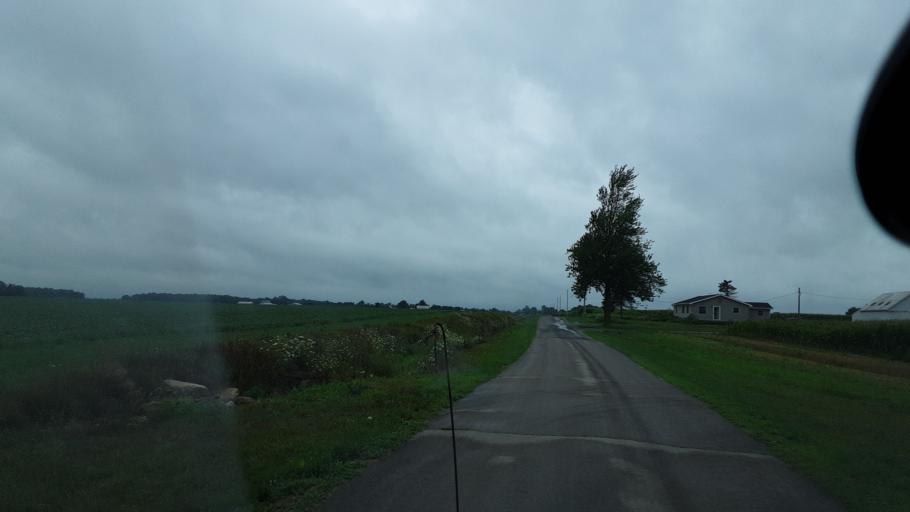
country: US
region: Ohio
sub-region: Van Wert County
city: Convoy
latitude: 40.8297
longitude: -84.7854
